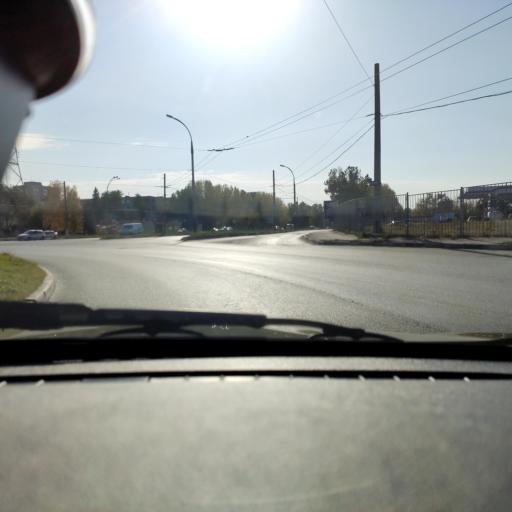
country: RU
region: Samara
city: Tol'yatti
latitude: 53.5305
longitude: 49.2608
